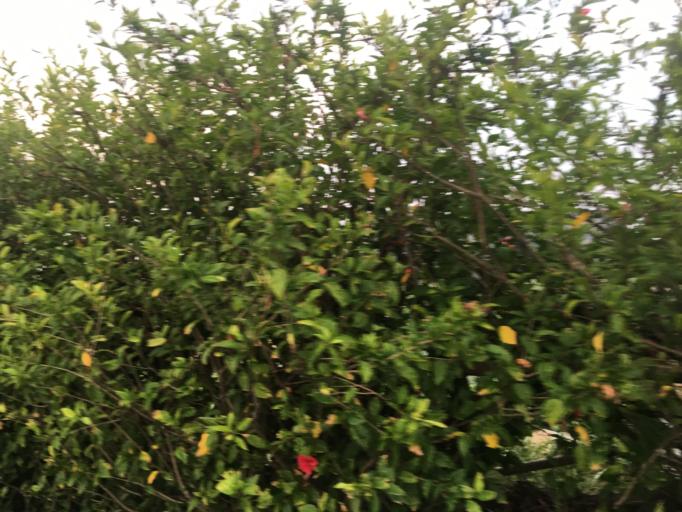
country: TW
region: Taiwan
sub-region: Hsinchu
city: Zhubei
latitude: 24.9177
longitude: 121.0065
